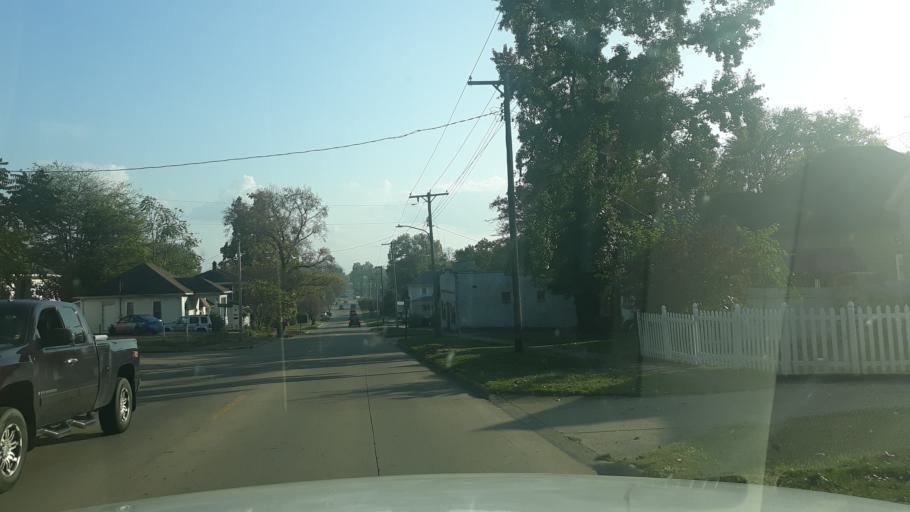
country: US
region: Illinois
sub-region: Saline County
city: Harrisburg
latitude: 37.7356
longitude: -88.5403
